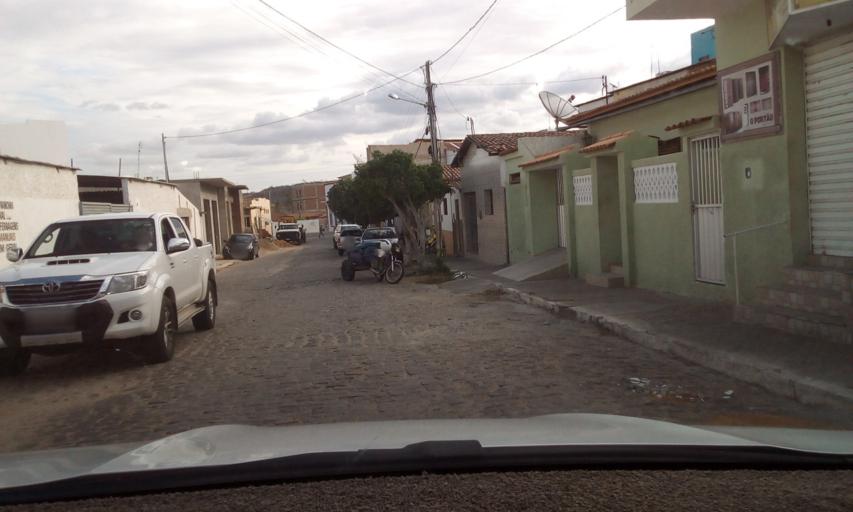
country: BR
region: Paraiba
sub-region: Picui
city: Picui
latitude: -6.5100
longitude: -36.3499
